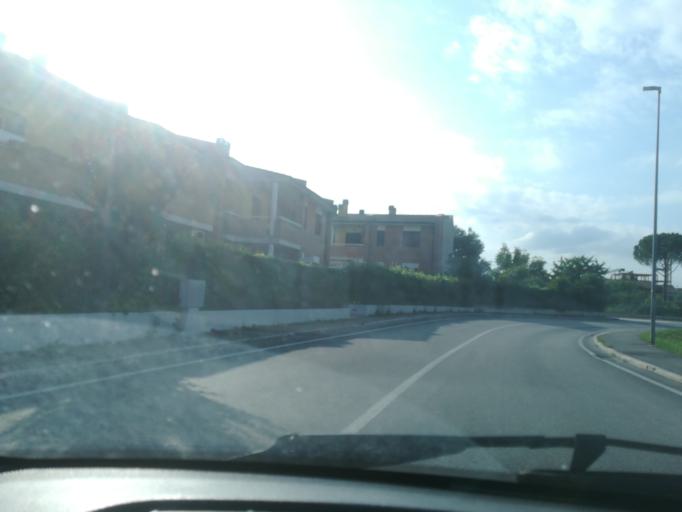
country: IT
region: The Marches
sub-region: Provincia di Macerata
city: Villa Potenza
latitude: 43.3214
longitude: 13.4246
